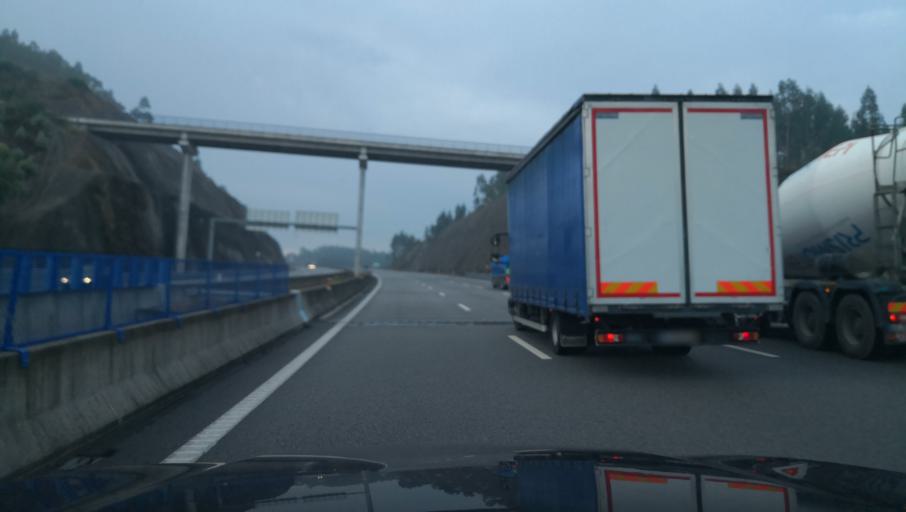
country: PT
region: Porto
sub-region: Paredes
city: Recarei
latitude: 41.1263
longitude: -8.4322
